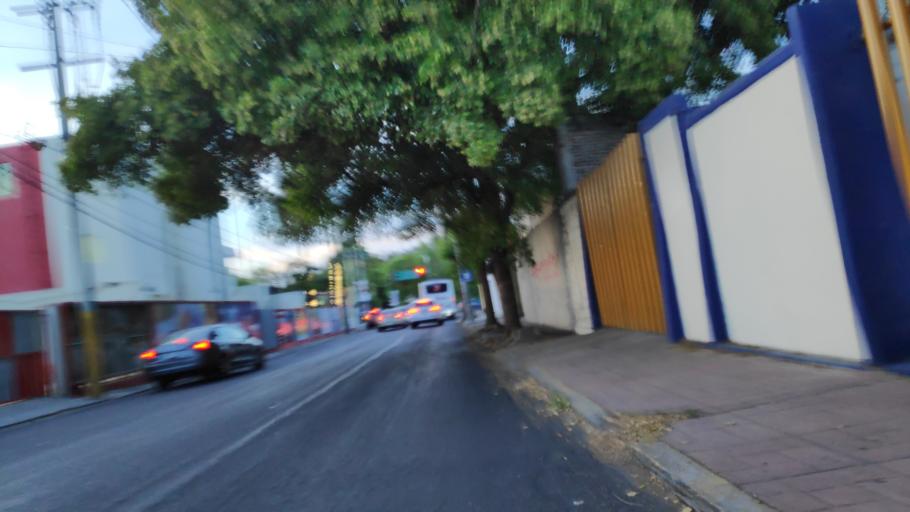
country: MX
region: Sinaloa
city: Culiacan
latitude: 24.8098
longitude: -107.4045
